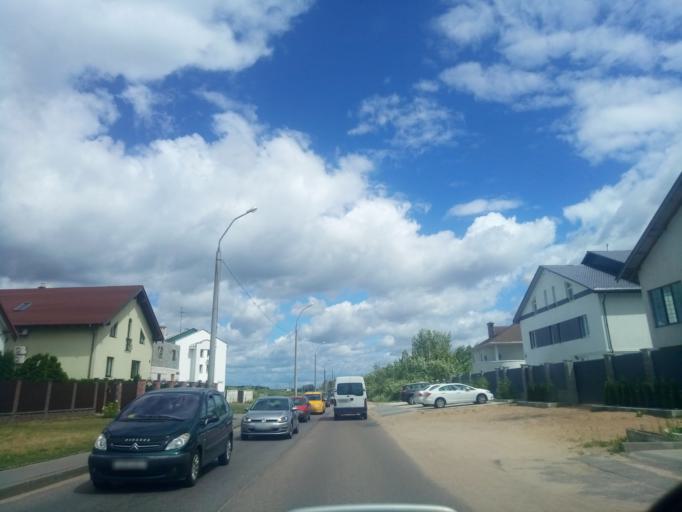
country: BY
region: Minsk
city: Zhdanovichy
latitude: 53.9370
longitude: 27.4335
